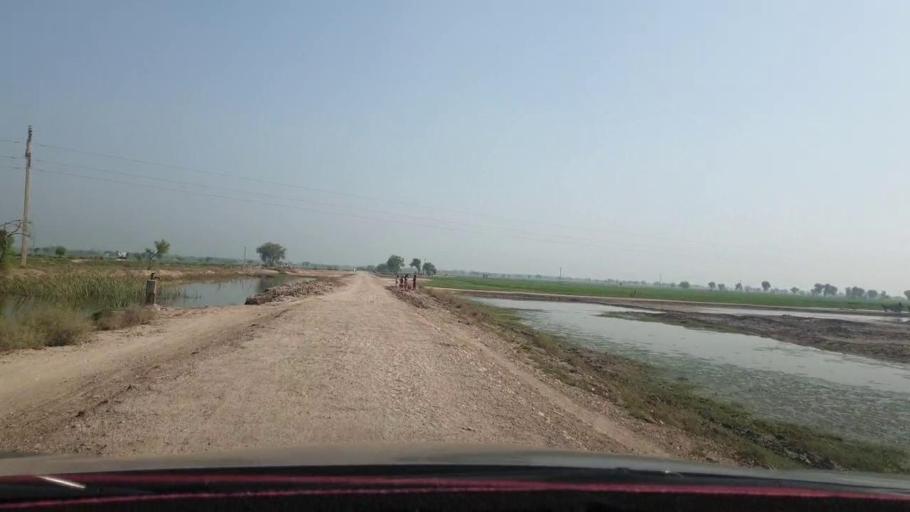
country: PK
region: Sindh
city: Nasirabad
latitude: 27.4952
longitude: 67.9299
